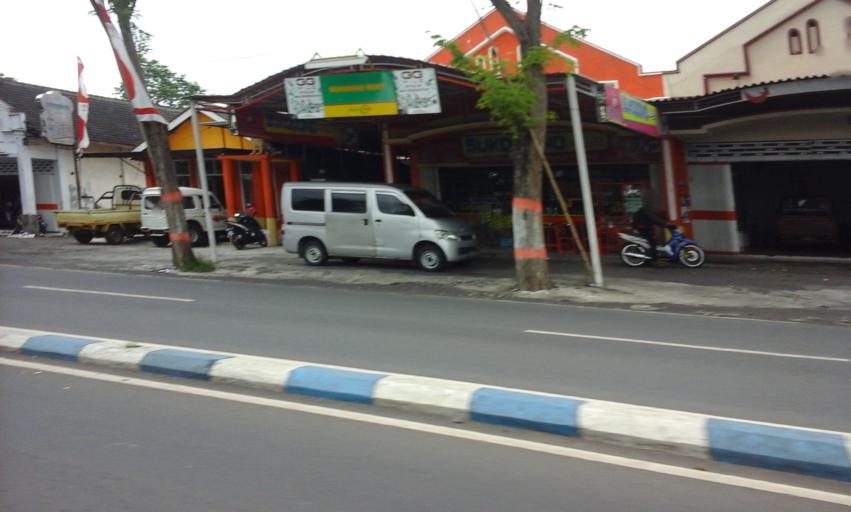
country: ID
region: East Java
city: Sukodono
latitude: -8.1001
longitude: 113.2337
